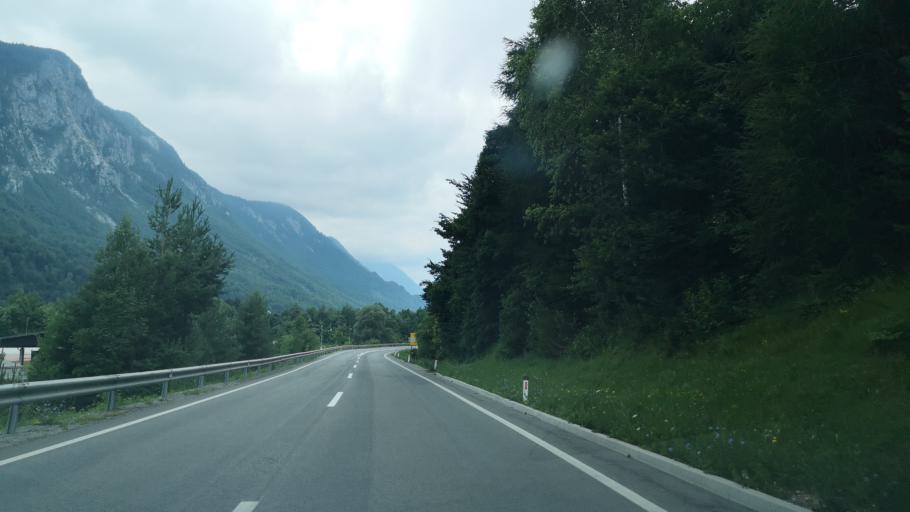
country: SI
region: Jesenice
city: Hrusica
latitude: 46.4448
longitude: 14.0294
